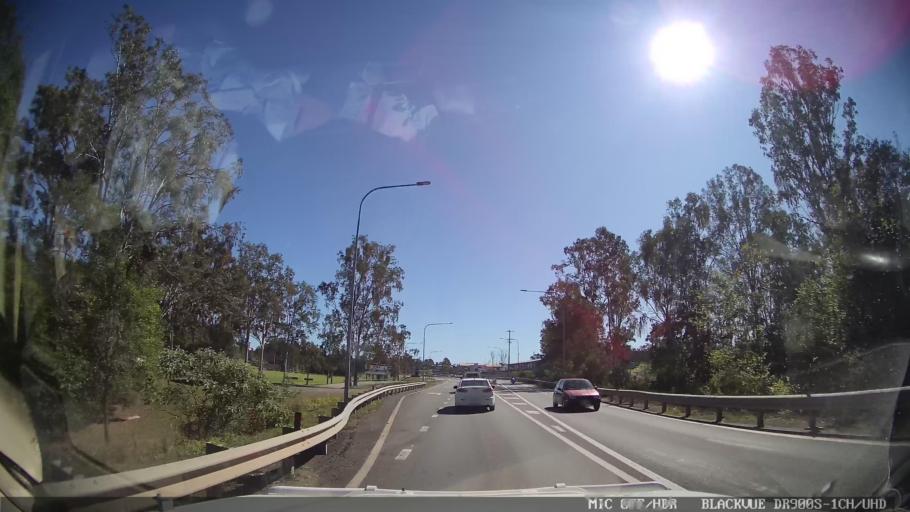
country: AU
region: Queensland
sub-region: Gympie Regional Council
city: Monkland
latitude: -26.2323
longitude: 152.6978
